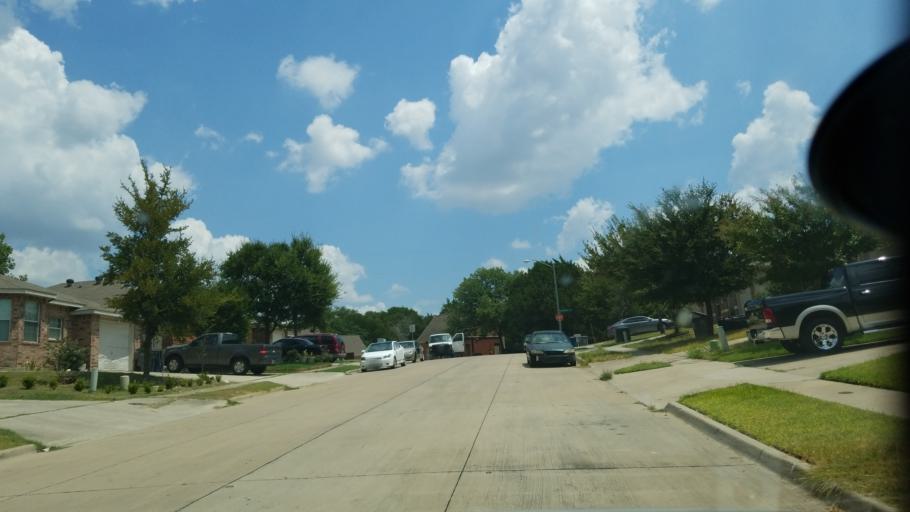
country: US
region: Texas
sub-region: Dallas County
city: Duncanville
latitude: 32.6834
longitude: -96.9048
